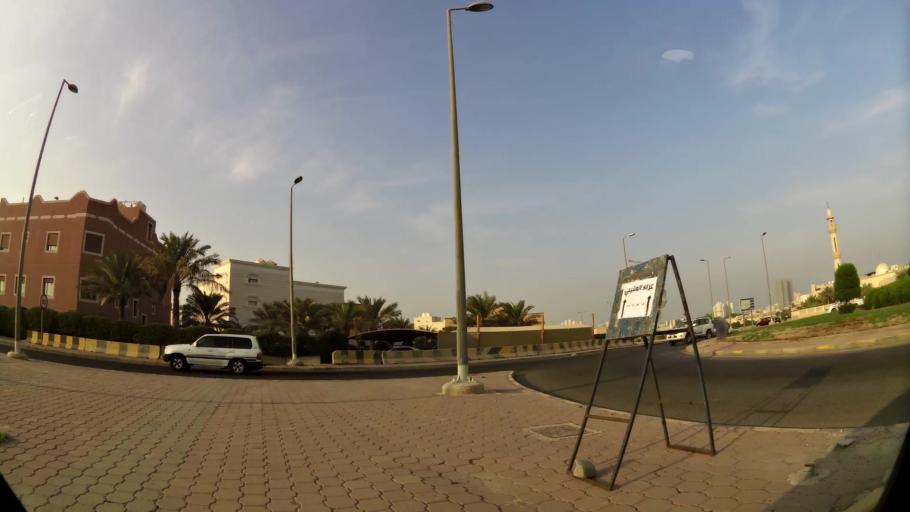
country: KW
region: Mubarak al Kabir
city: Sabah as Salim
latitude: 29.2499
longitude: 48.0708
